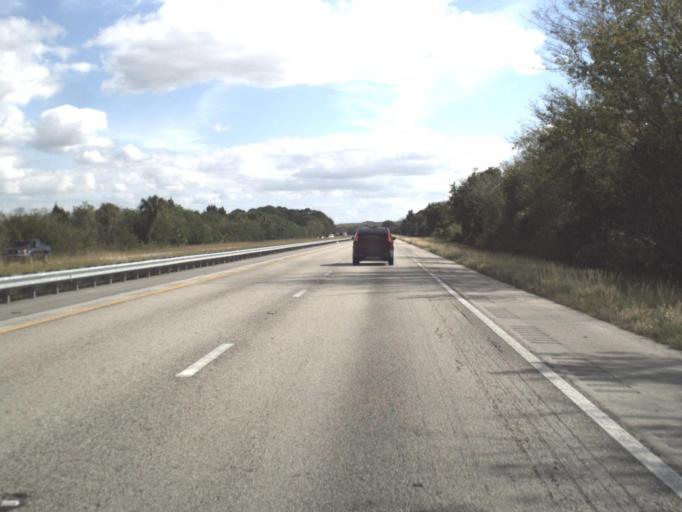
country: US
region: Florida
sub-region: Brevard County
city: Port Saint John
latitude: 28.4219
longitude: -80.8470
